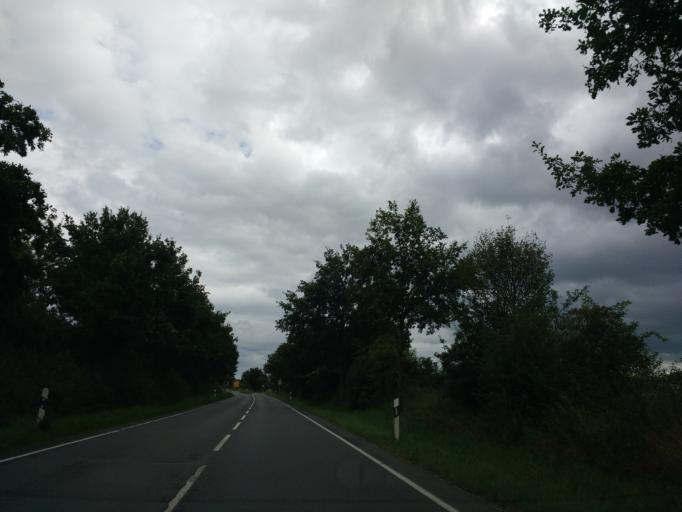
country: DE
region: Lower Saxony
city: Bad Laer
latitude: 52.0975
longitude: 8.0789
